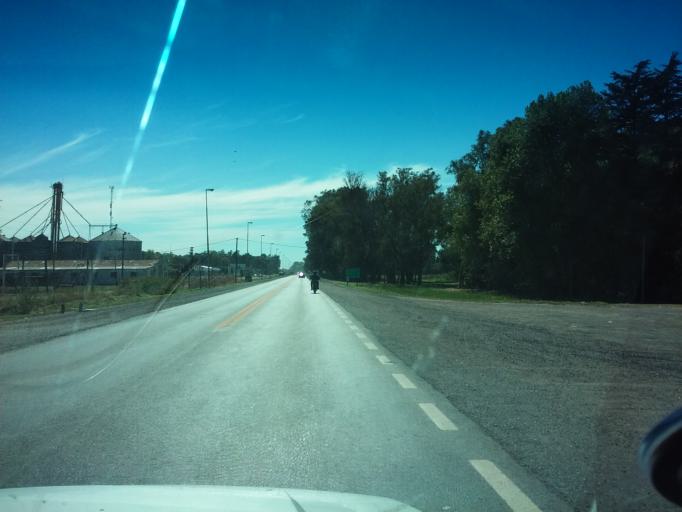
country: AR
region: Buenos Aires
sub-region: Partido de Nueve de Julio
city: Nueve de Julio
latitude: -35.4742
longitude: -60.8614
